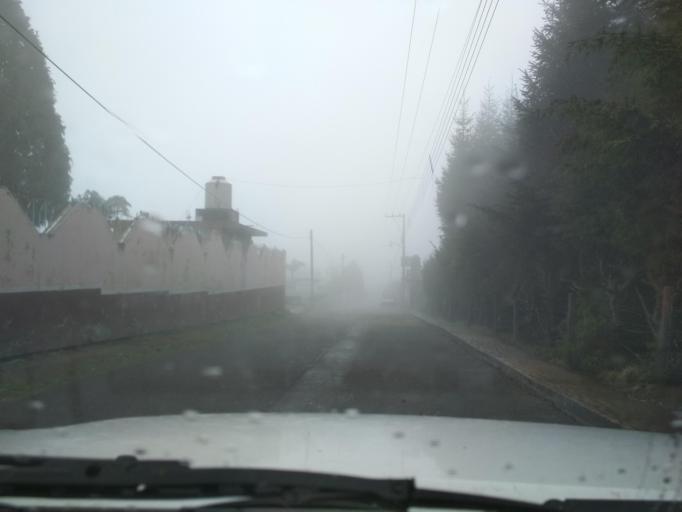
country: MX
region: Veracruz
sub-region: Mariano Escobedo
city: San Isidro el Berro
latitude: 18.9272
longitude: -97.2072
